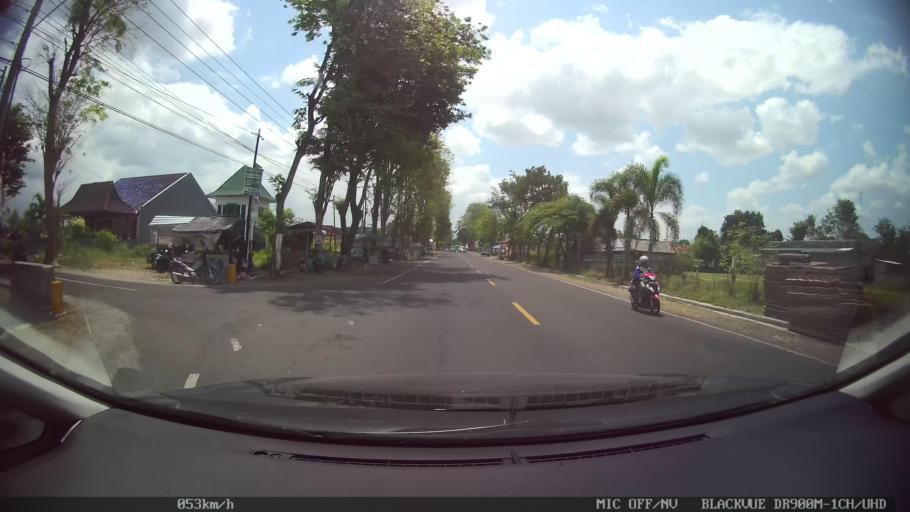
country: ID
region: Daerah Istimewa Yogyakarta
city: Bantul
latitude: -7.8991
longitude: 110.3461
